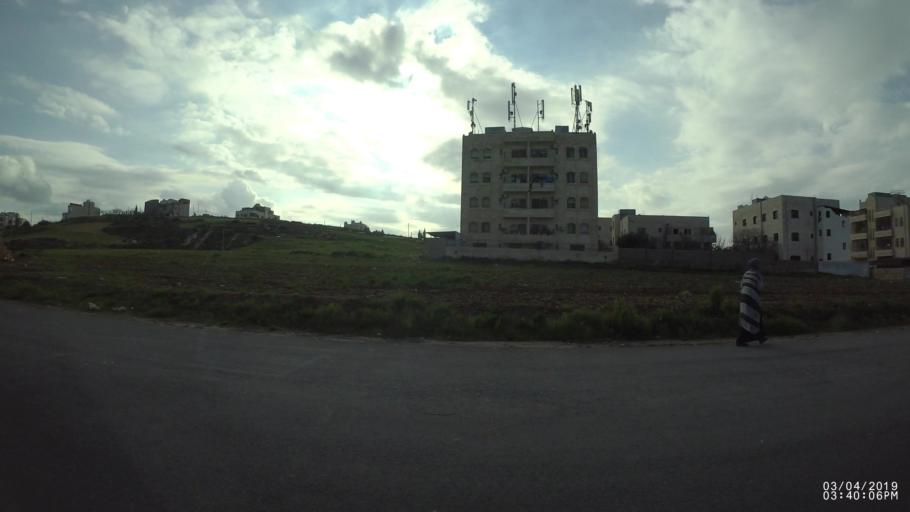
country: JO
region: Amman
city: Umm as Summaq
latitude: 31.9136
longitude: 35.8502
